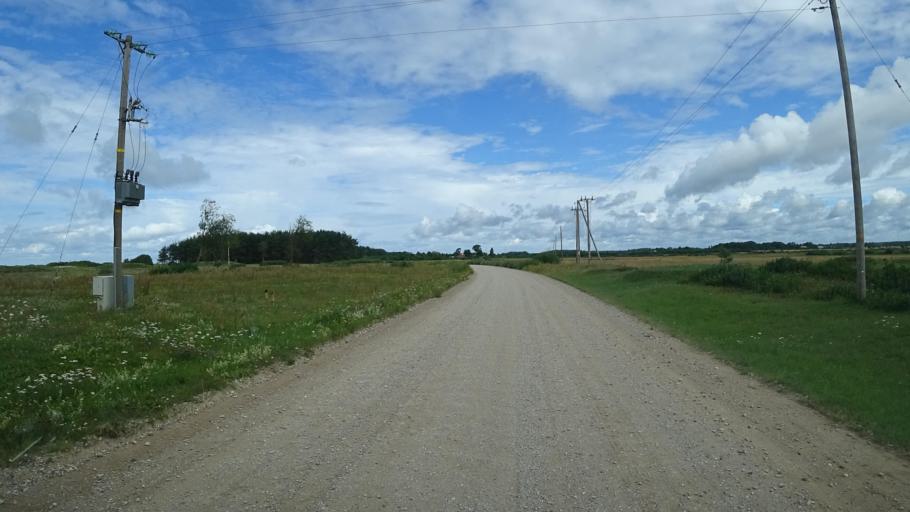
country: LV
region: Liepaja
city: Vec-Liepaja
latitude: 56.6426
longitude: 21.0449
